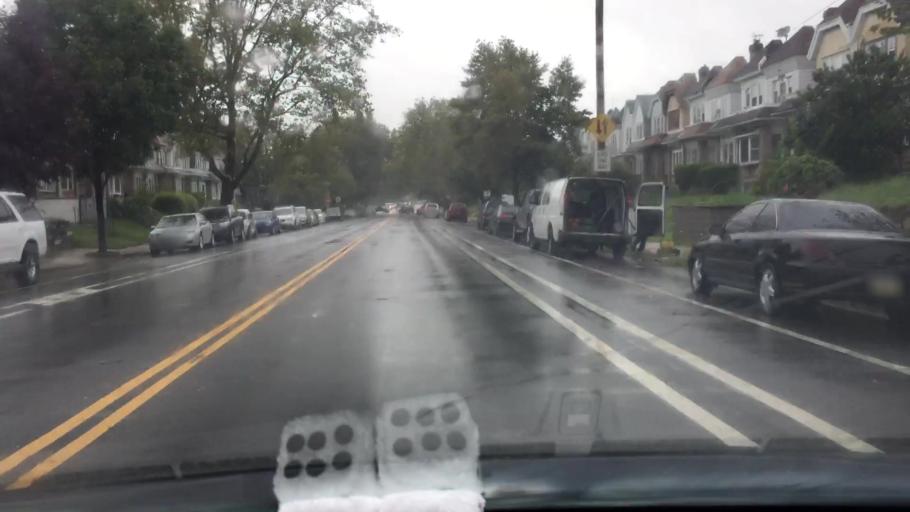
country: US
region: New Jersey
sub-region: Burlington County
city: Palmyra
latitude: 40.0384
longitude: -75.0418
